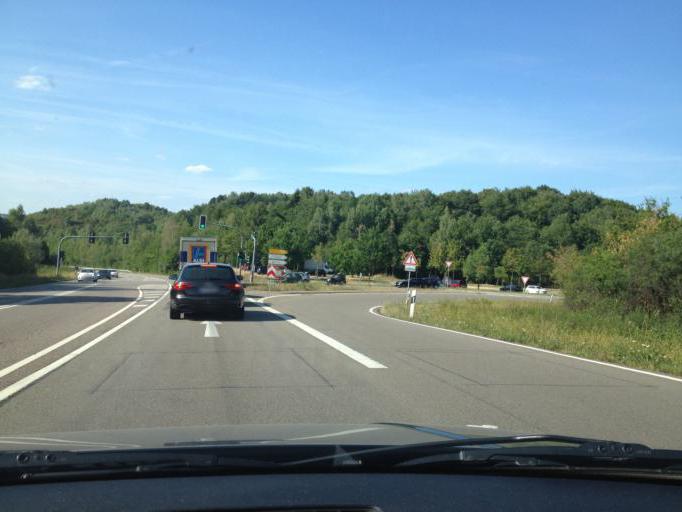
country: DE
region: Saarland
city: Neunkirchen
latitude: 49.3318
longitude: 7.1606
